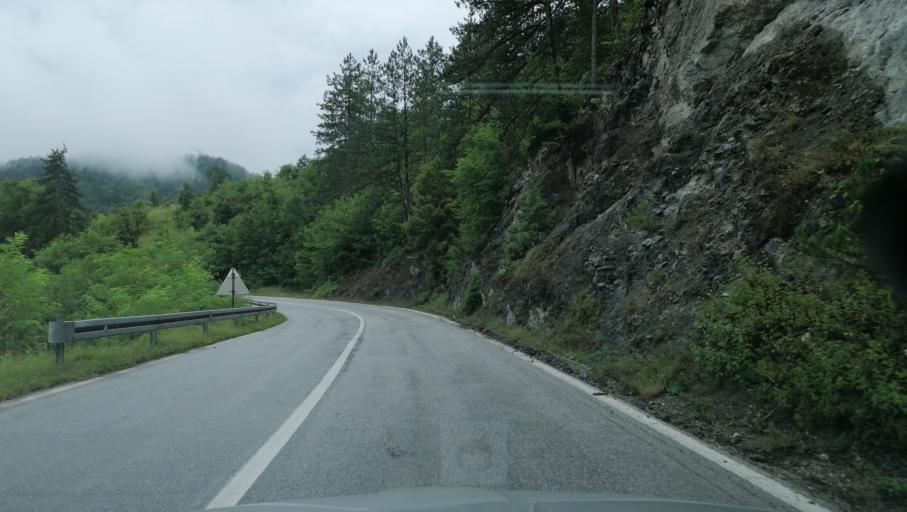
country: BA
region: Republika Srpska
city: Visegrad
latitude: 43.7874
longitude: 19.3252
